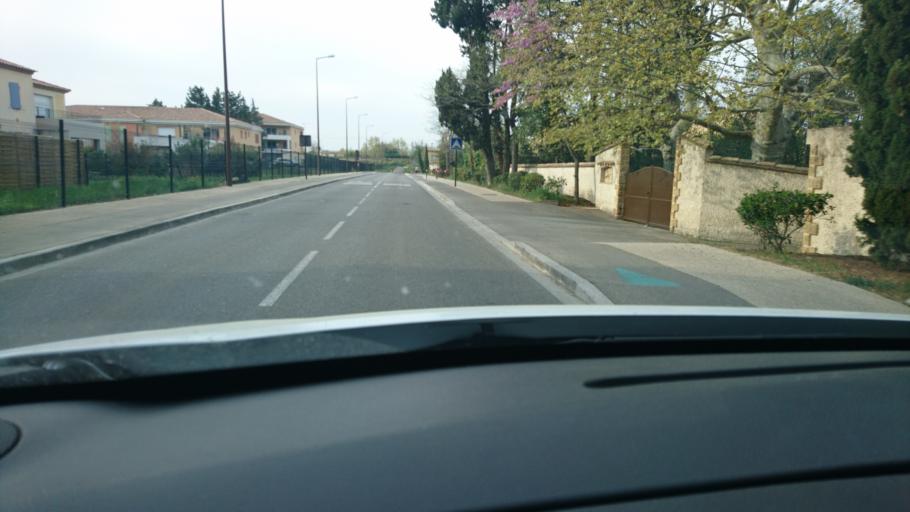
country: FR
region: Provence-Alpes-Cote d'Azur
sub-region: Departement du Vaucluse
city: Montfavet
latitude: 43.9313
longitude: 4.8813
